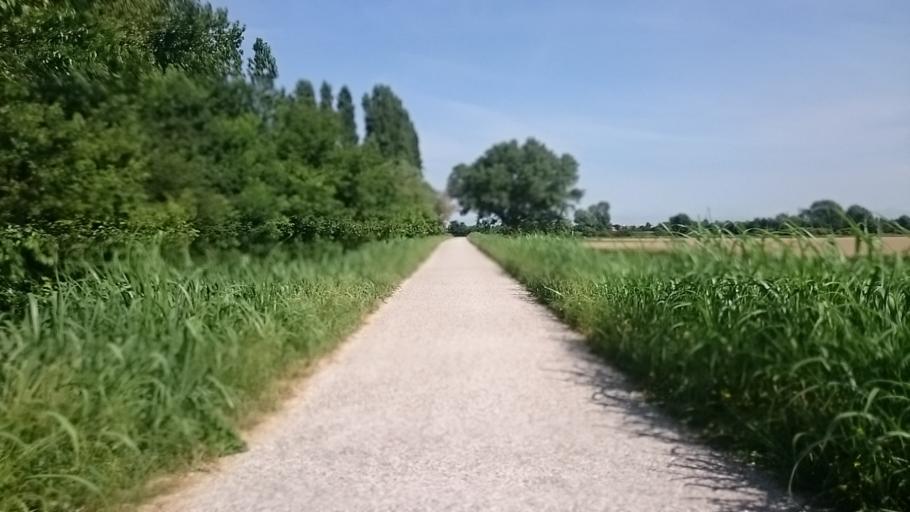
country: IT
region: Veneto
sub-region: Provincia di Padova
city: Selvazzano Dentro
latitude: 45.3932
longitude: 11.7863
